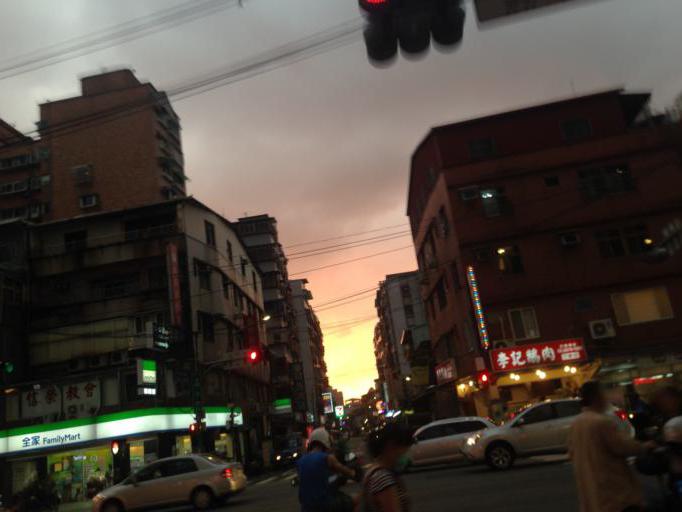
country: TW
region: Taiwan
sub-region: Taoyuan
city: Taoyuan
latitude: 24.9362
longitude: 121.3759
